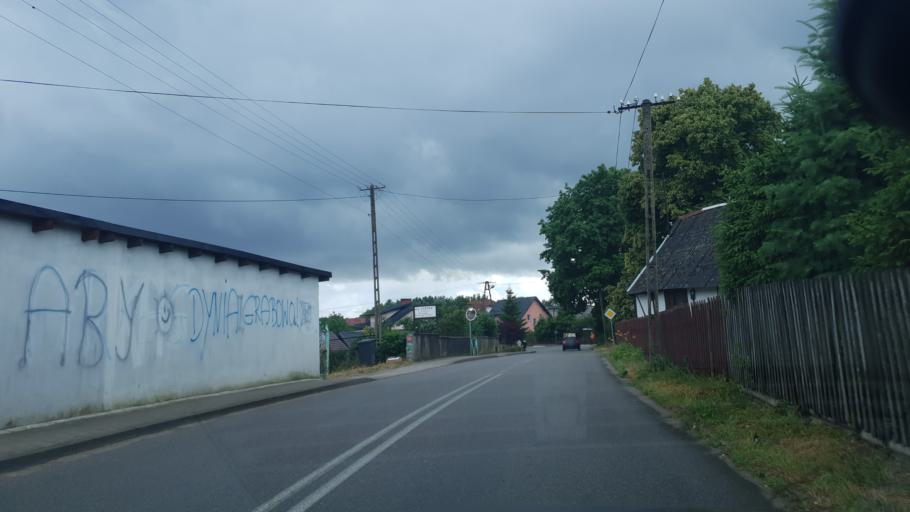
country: PL
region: Pomeranian Voivodeship
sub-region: Powiat kartuski
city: Stezyca
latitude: 54.2371
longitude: 17.9863
